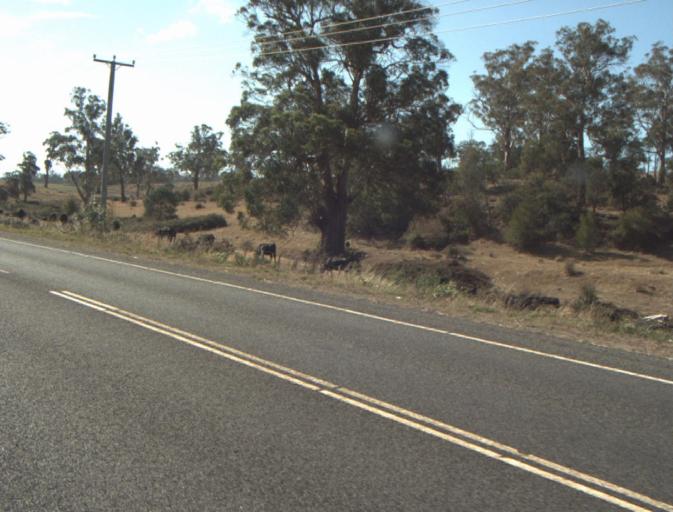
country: AU
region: Tasmania
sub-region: Launceston
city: Mayfield
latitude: -41.3458
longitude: 147.0948
